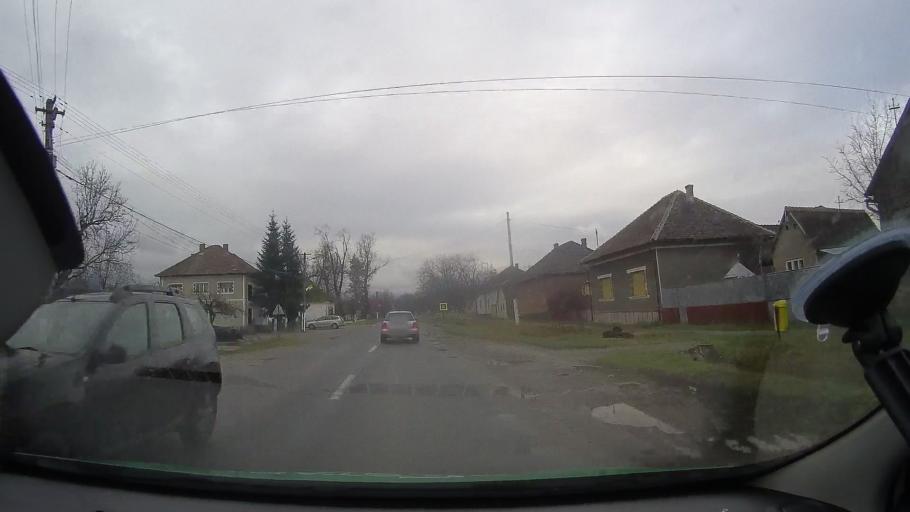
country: RO
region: Arad
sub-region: Comuna Buteni
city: Buteni
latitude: 46.3305
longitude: 22.1249
